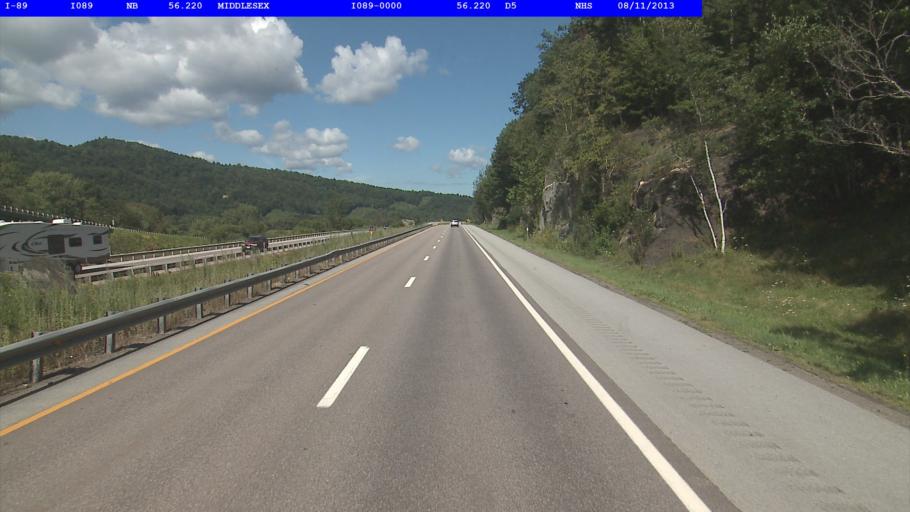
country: US
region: Vermont
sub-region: Washington County
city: Montpelier
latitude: 44.2759
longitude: -72.6484
